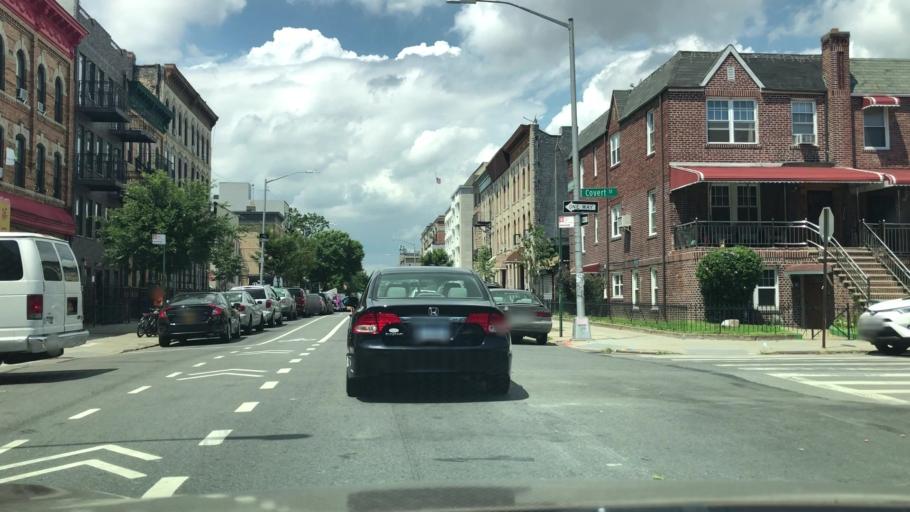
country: US
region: New York
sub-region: Kings County
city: East New York
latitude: 40.6921
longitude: -73.9065
